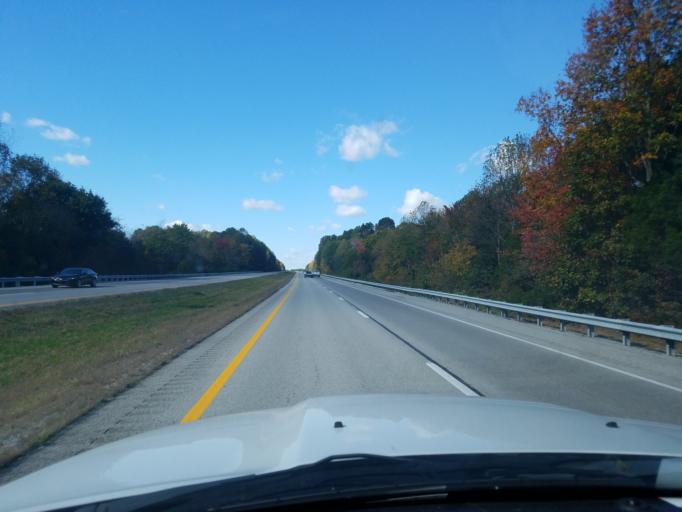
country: US
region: Kentucky
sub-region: Barren County
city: Glasgow
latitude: 36.9974
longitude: -85.8017
